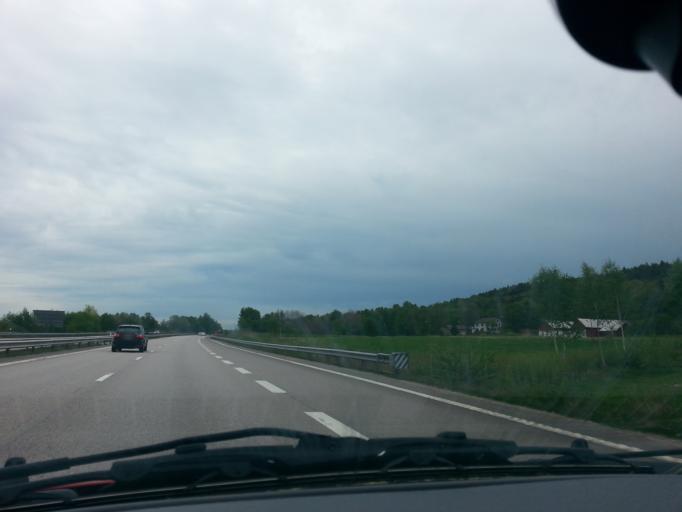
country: SE
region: Vaestra Goetaland
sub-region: Lerums Kommun
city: Lerum
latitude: 57.7759
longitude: 12.2972
